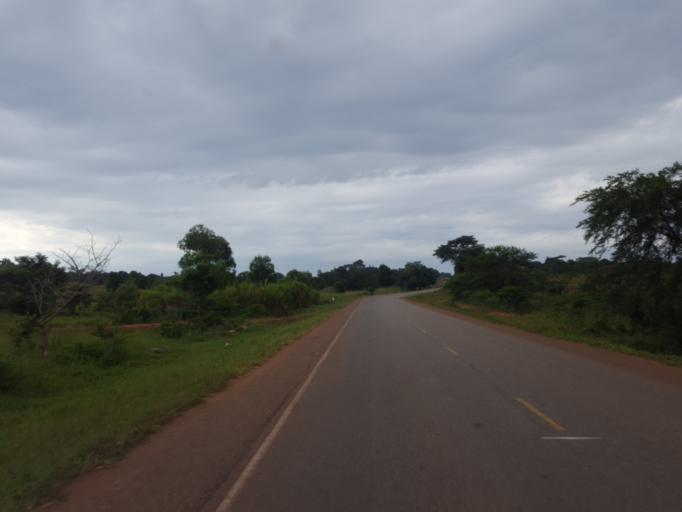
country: UG
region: Central Region
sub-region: Kiboga District
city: Kiboga
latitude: 1.0183
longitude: 31.6884
